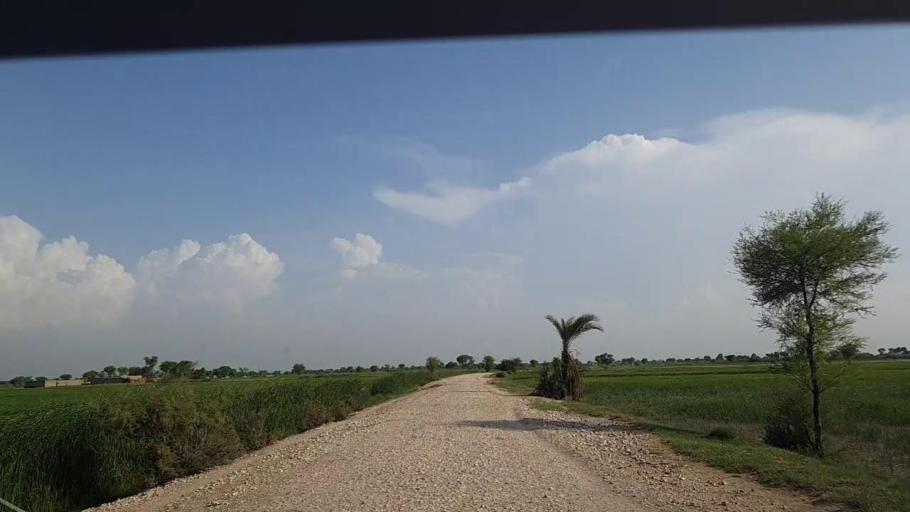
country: PK
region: Sindh
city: Khanpur
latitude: 27.8505
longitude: 69.3776
